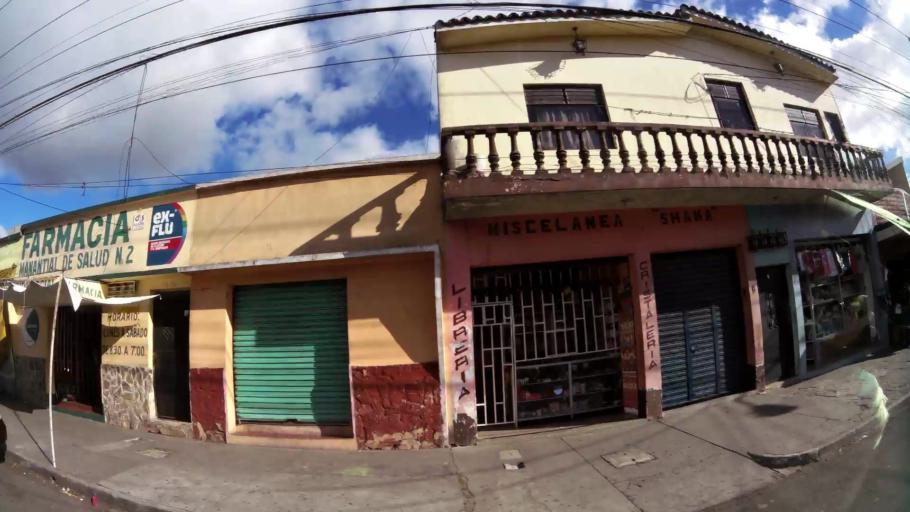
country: GT
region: Guatemala
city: Guatemala City
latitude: 14.6168
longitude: -90.5454
